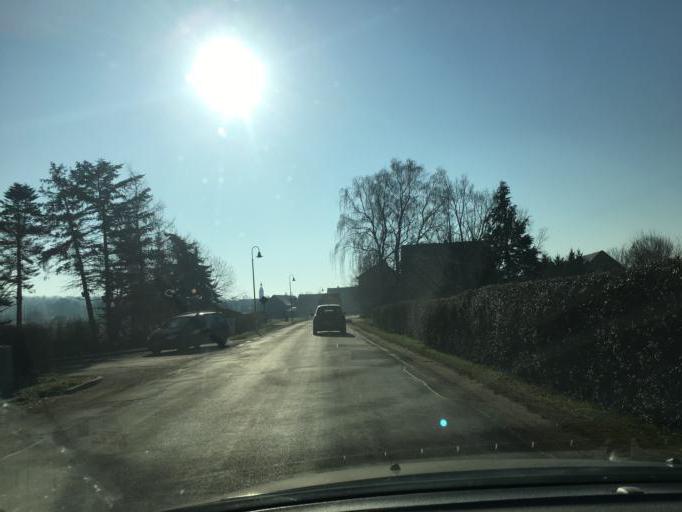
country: DE
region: Saxony
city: Otterwisch
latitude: 51.2100
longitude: 12.6053
